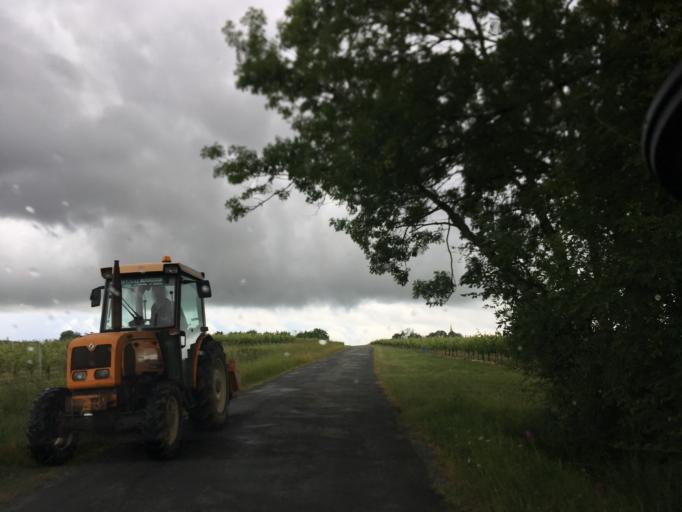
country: FR
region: Aquitaine
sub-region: Departement de la Gironde
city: Vertheuil
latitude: 45.3123
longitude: -0.8320
